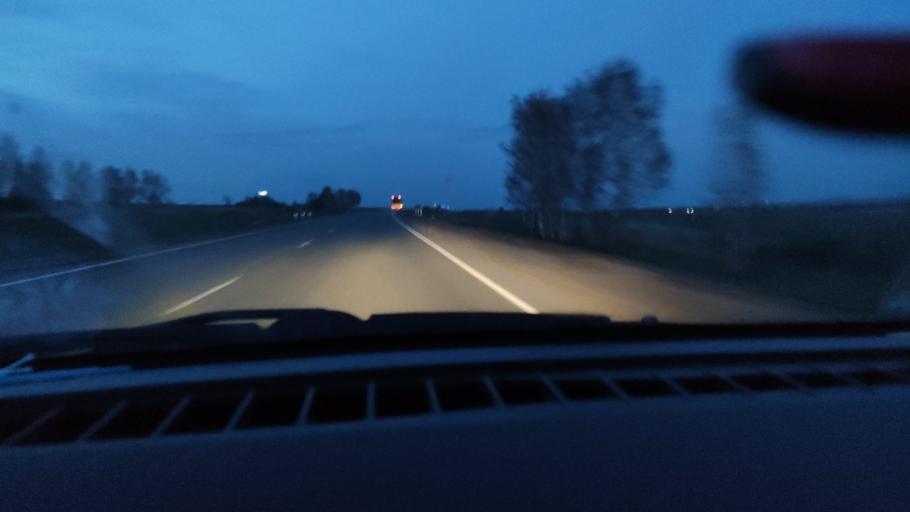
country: RU
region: Saratov
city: Sennoy
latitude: 52.1359
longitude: 46.8724
